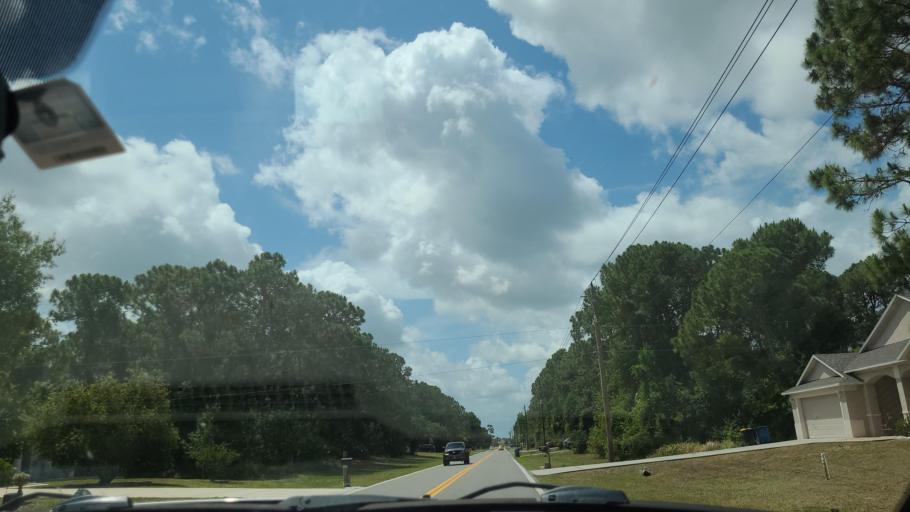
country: US
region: Florida
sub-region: Brevard County
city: June Park
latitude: 28.0049
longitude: -80.7167
